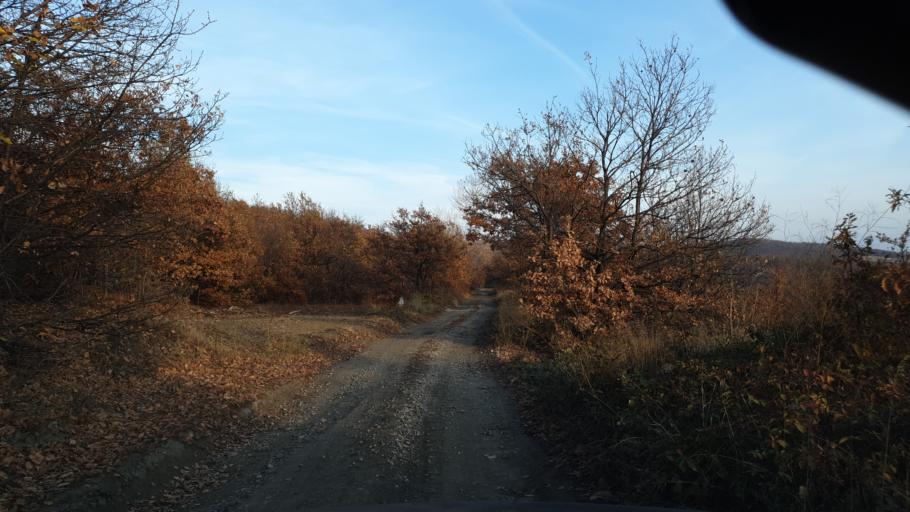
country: RS
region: Central Serbia
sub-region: Borski Okrug
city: Bor
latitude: 44.0729
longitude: 22.0672
